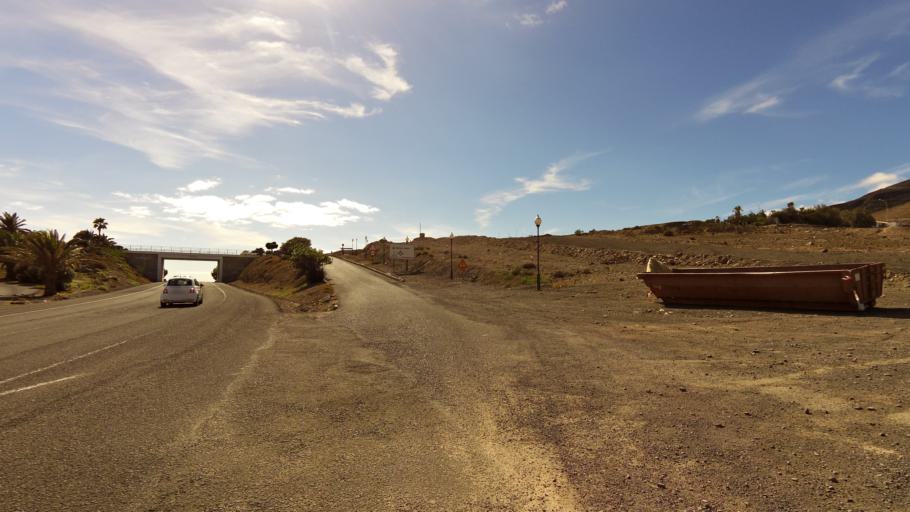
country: ES
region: Canary Islands
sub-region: Provincia de Las Palmas
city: Pajara
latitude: 28.0603
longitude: -14.3200
